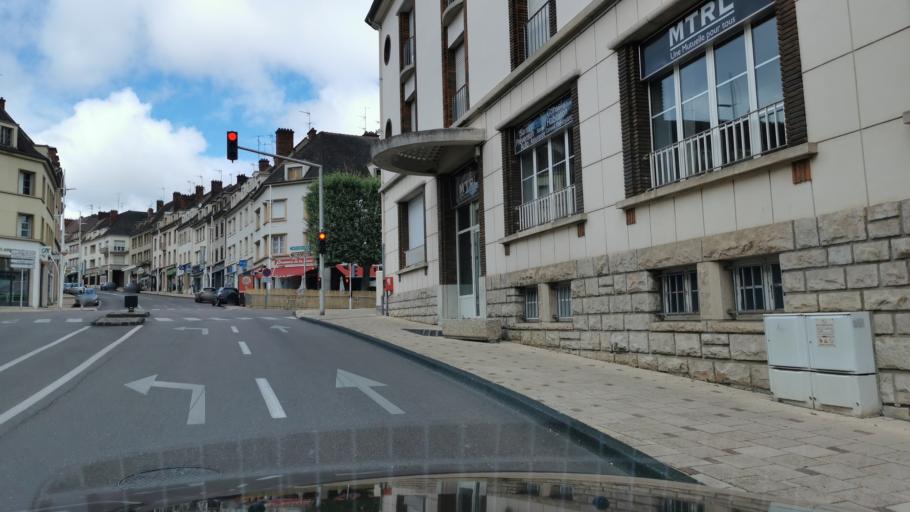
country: FR
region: Bourgogne
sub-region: Departement de Saone-et-Loire
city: Le Creusot
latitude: 46.8066
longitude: 4.4288
